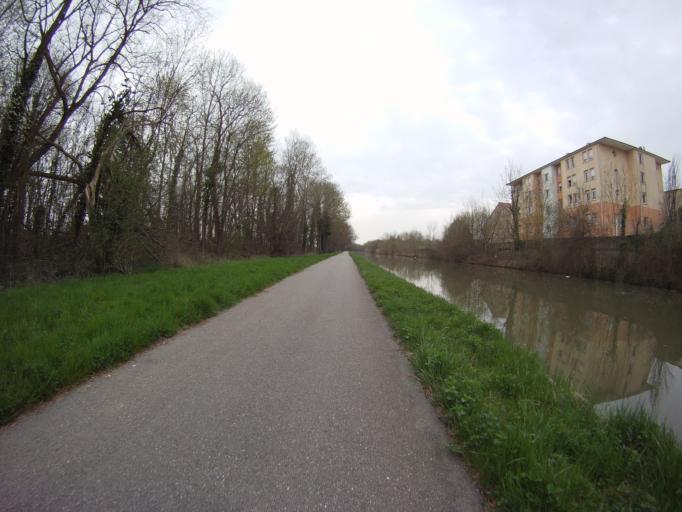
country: FR
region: Lorraine
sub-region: Departement de Meurthe-et-Moselle
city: Jarville-la-Malgrange
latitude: 48.6667
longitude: 6.2163
